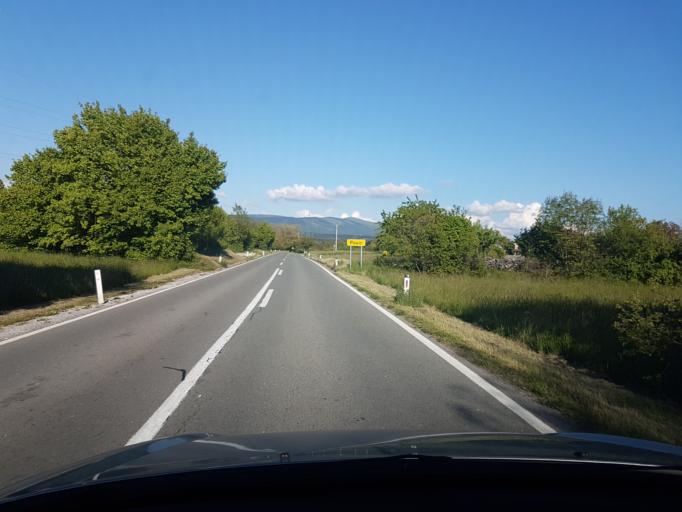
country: SI
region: Divaca
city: Divaca
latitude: 45.7024
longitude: 13.9299
